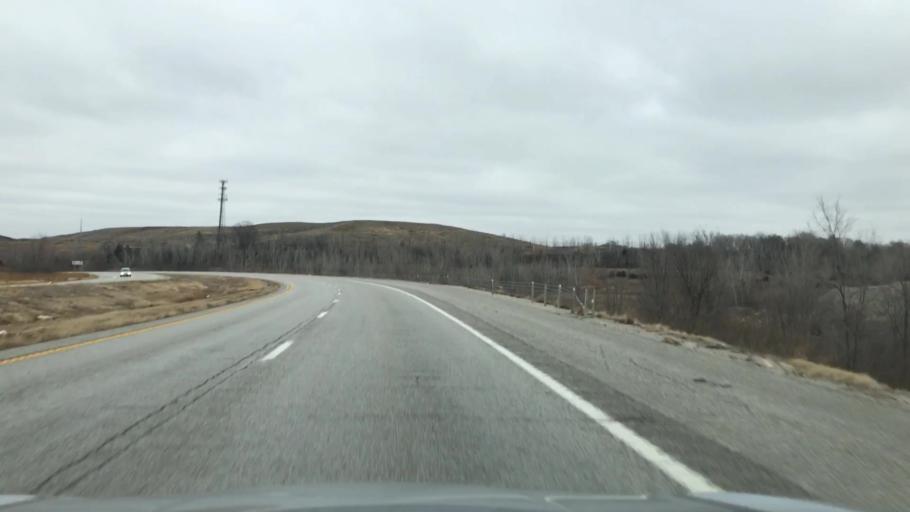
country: US
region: Missouri
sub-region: Jackson County
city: East Independence
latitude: 39.1306
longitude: -94.3838
